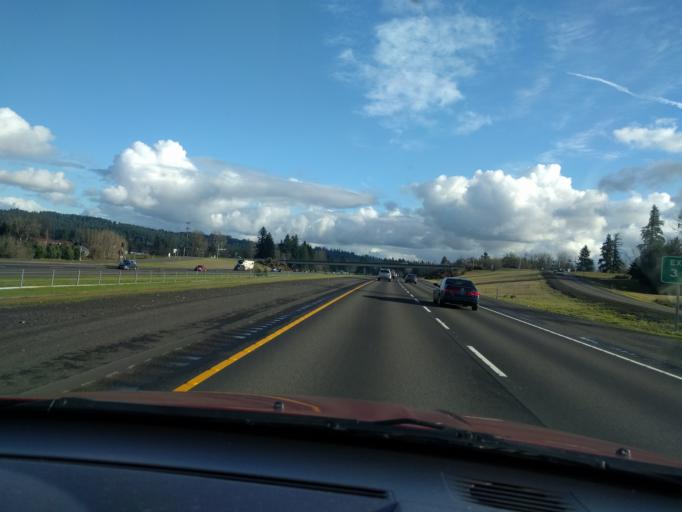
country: US
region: Oregon
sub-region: Clackamas County
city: Stafford
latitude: 45.3711
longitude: -122.7101
